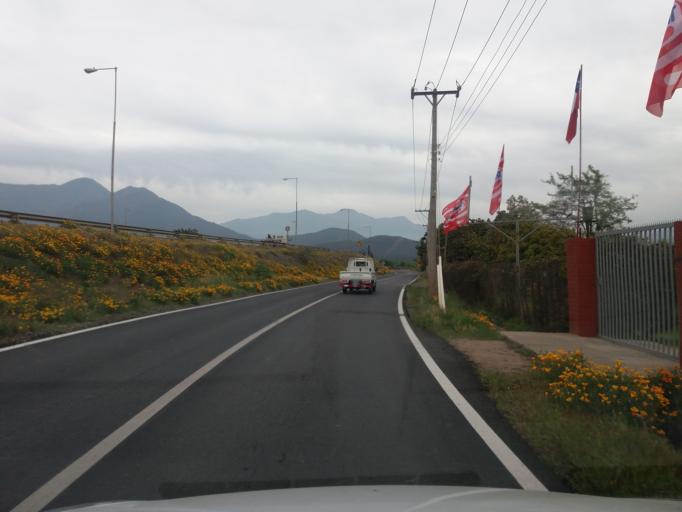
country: CL
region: Valparaiso
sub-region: Provincia de Quillota
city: Hacienda La Calera
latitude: -32.8411
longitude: -71.1109
